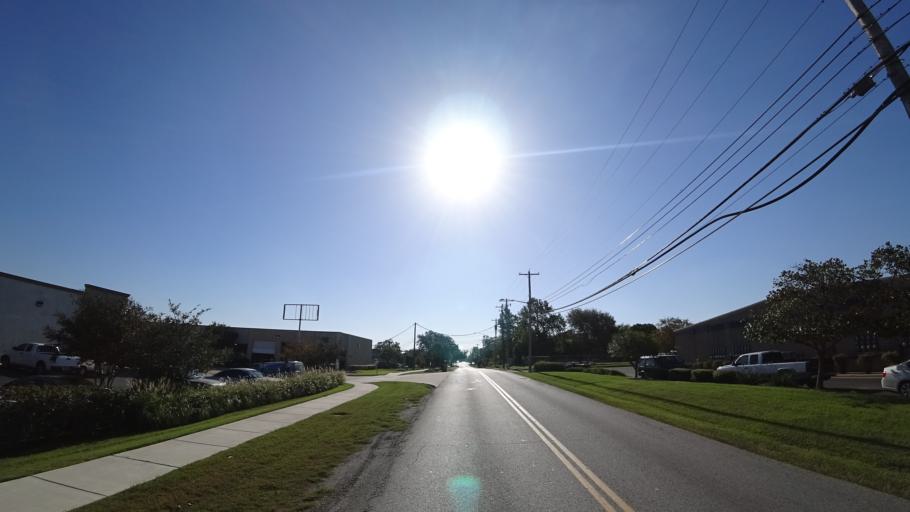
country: US
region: Texas
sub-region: Travis County
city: Austin
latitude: 30.3486
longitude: -97.7057
